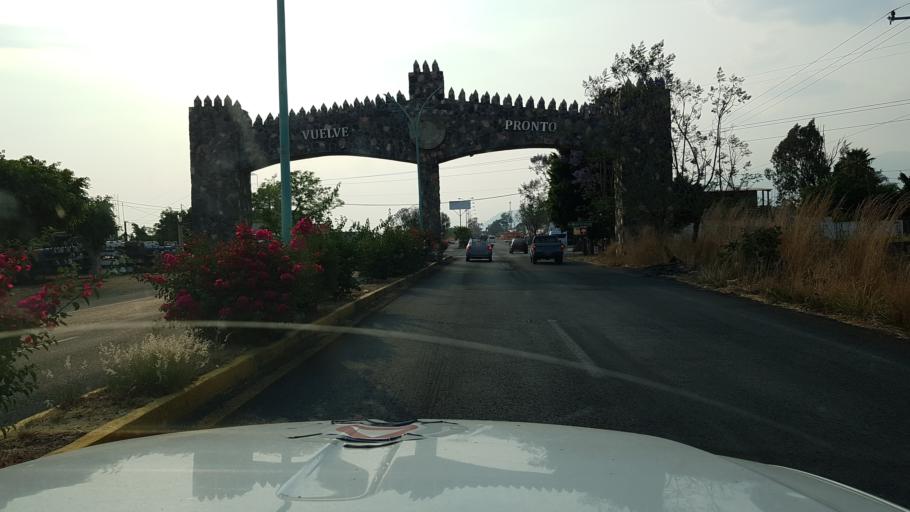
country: MX
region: Morelos
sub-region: Atlatlahucan
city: Colonia San Francisco
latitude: 18.8946
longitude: -98.9020
